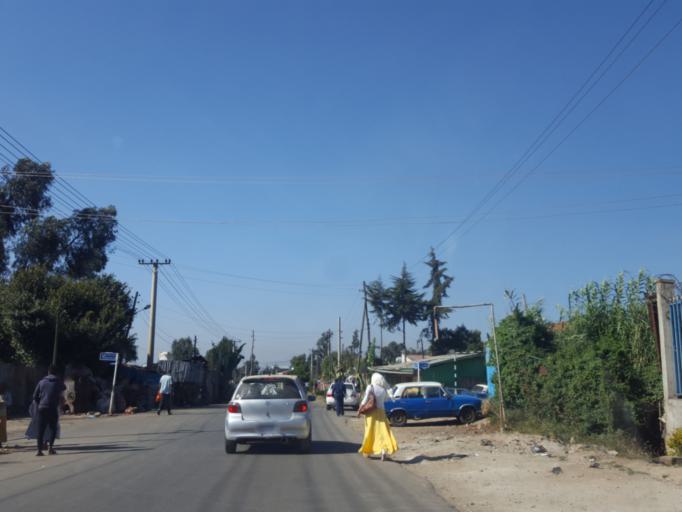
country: ET
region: Adis Abeba
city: Addis Ababa
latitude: 9.0521
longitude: 38.7389
